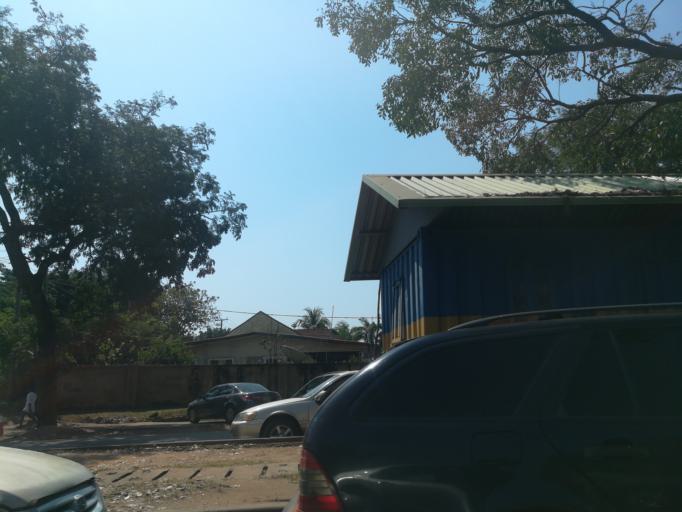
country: NG
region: Abuja Federal Capital Territory
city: Abuja
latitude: 9.0546
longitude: 7.4561
